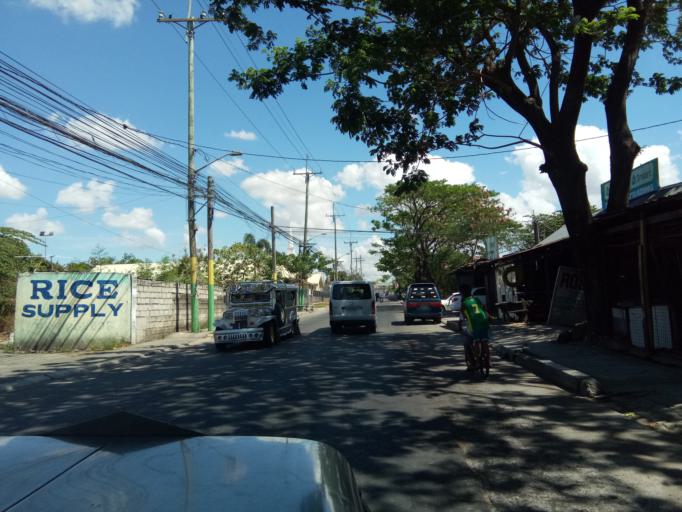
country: PH
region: Calabarzon
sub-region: Province of Cavite
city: Dasmarinas
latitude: 14.3431
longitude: 120.9474
